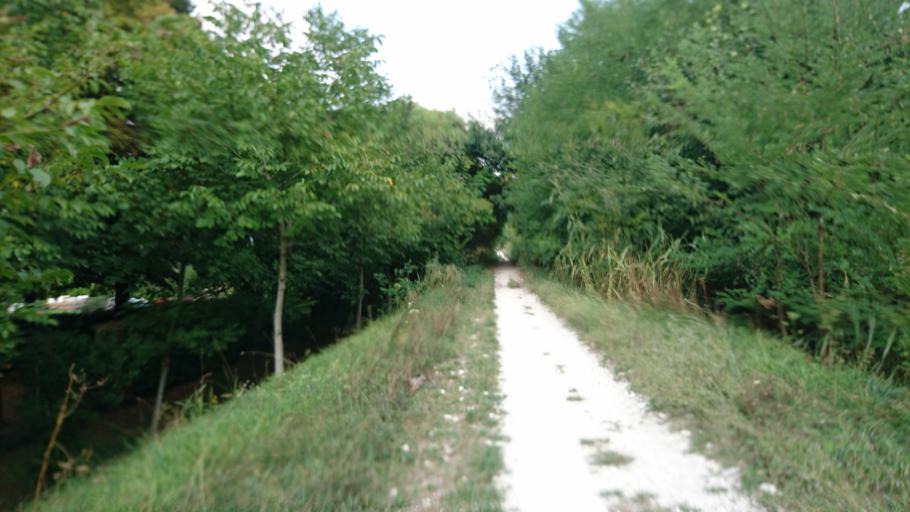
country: IT
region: Veneto
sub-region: Provincia di Padova
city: Saletto
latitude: 45.4580
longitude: 11.8608
